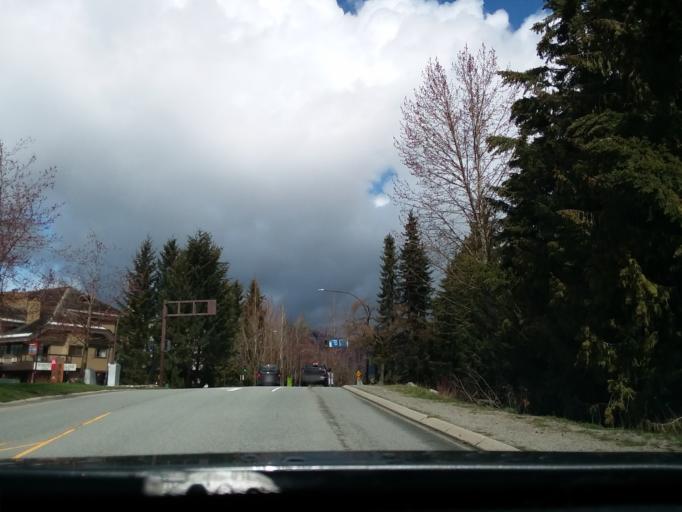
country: CA
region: British Columbia
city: Whistler
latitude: 50.1144
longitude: -122.9527
